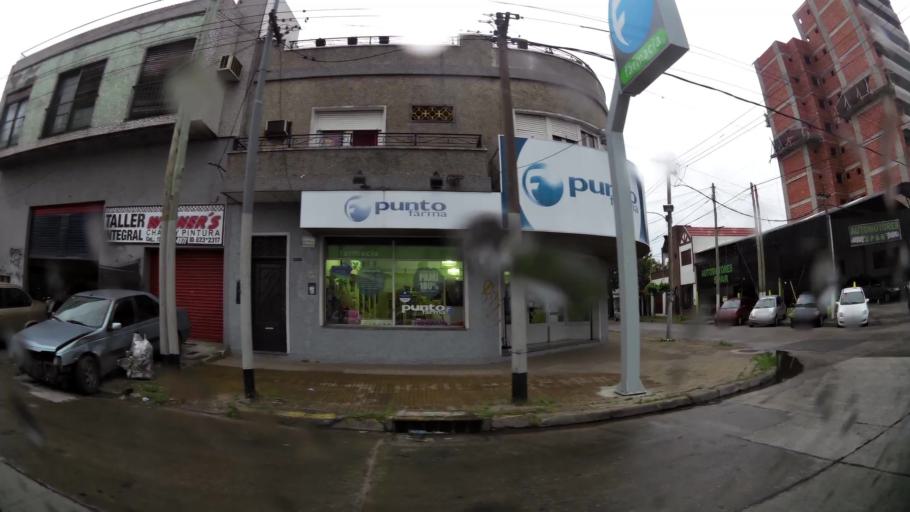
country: AR
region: Buenos Aires
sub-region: Partido de Lanus
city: Lanus
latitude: -34.6953
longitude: -58.4074
